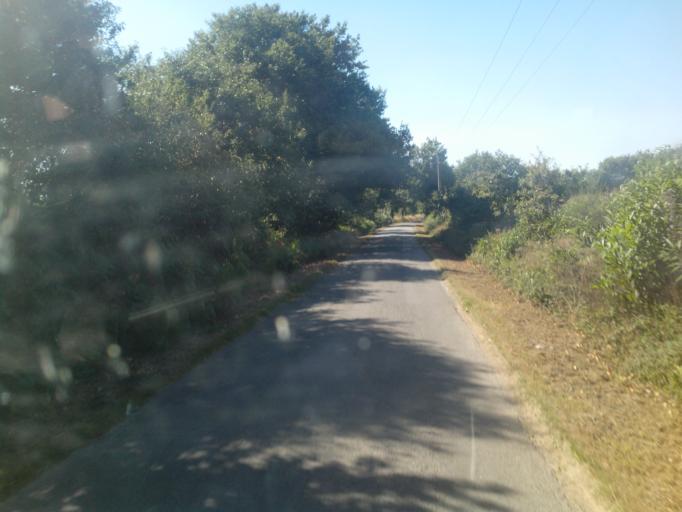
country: FR
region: Brittany
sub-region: Departement du Morbihan
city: Molac
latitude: 47.7298
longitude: -2.4094
